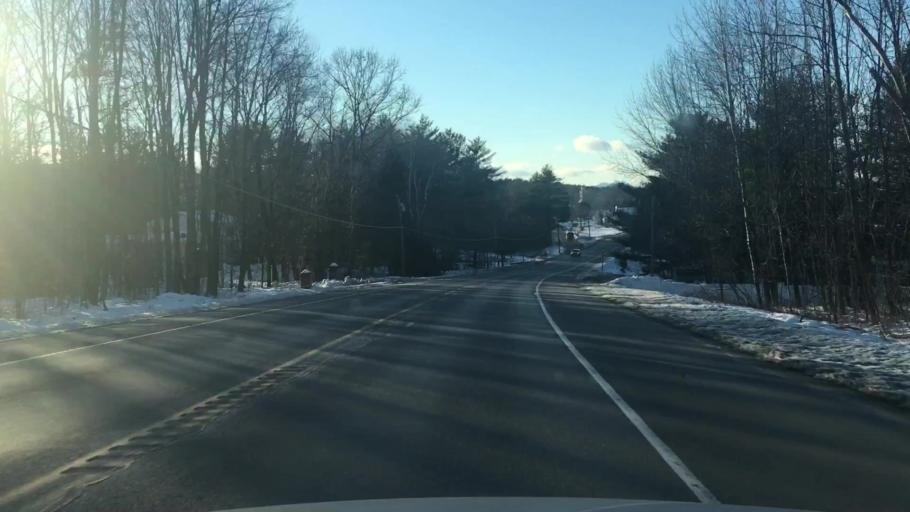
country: US
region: Maine
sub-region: Franklin County
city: New Sharon
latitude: 44.6364
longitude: -70.0041
